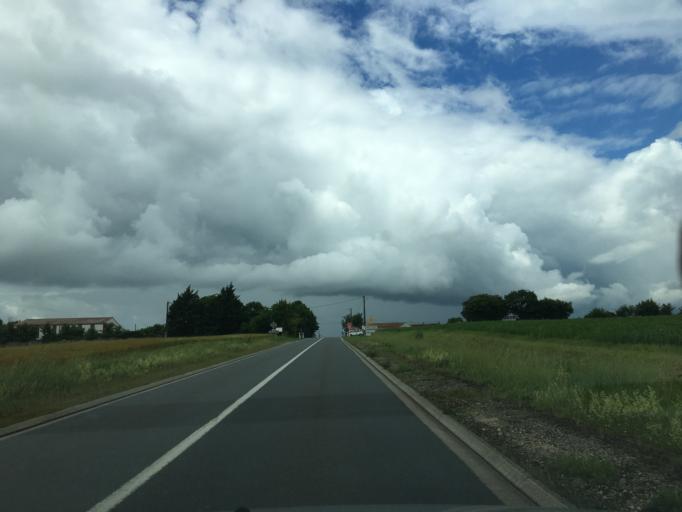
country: FR
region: Poitou-Charentes
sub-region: Departement des Deux-Sevres
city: Beauvoir-sur-Niort
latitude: 46.0707
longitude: -0.5072
